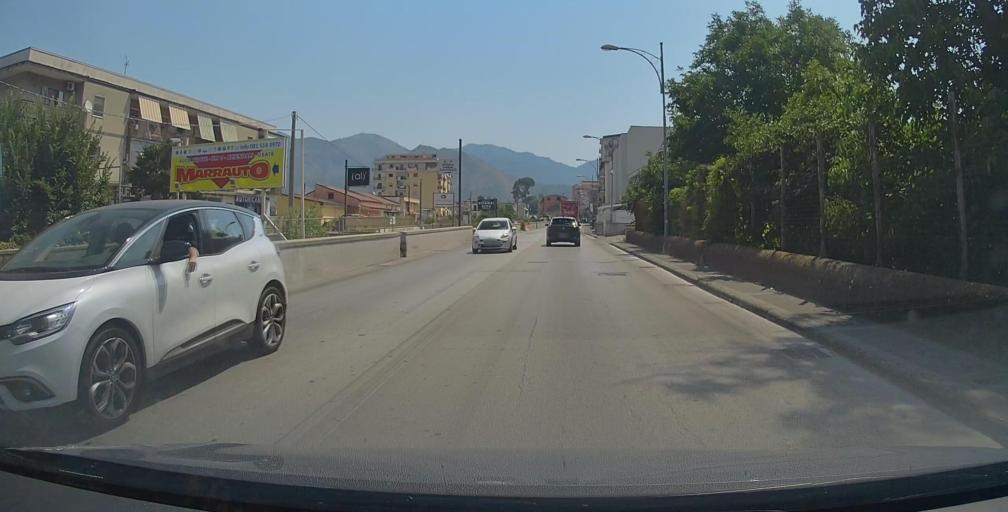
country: IT
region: Campania
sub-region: Provincia di Salerno
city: Nocera Superiore
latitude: 40.7406
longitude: 14.6590
